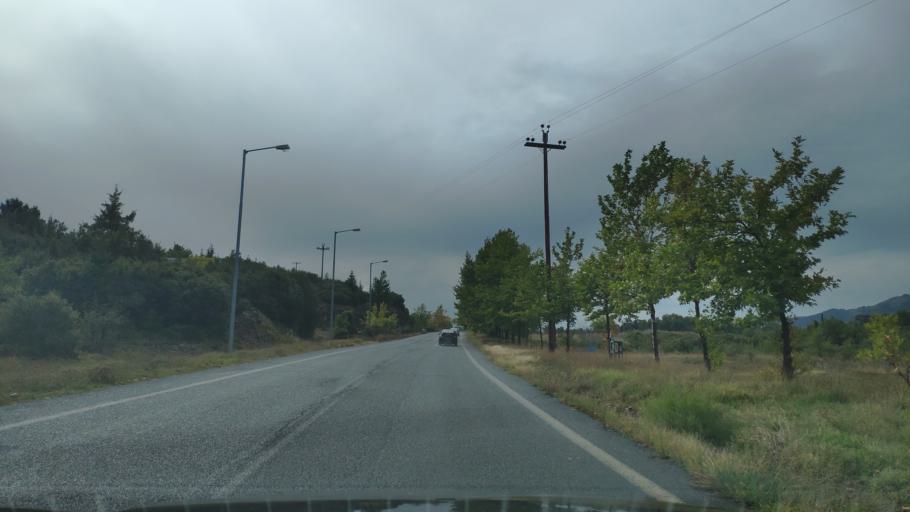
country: GR
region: Peloponnese
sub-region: Nomos Arkadias
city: Langadhia
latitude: 37.6798
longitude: 22.1917
